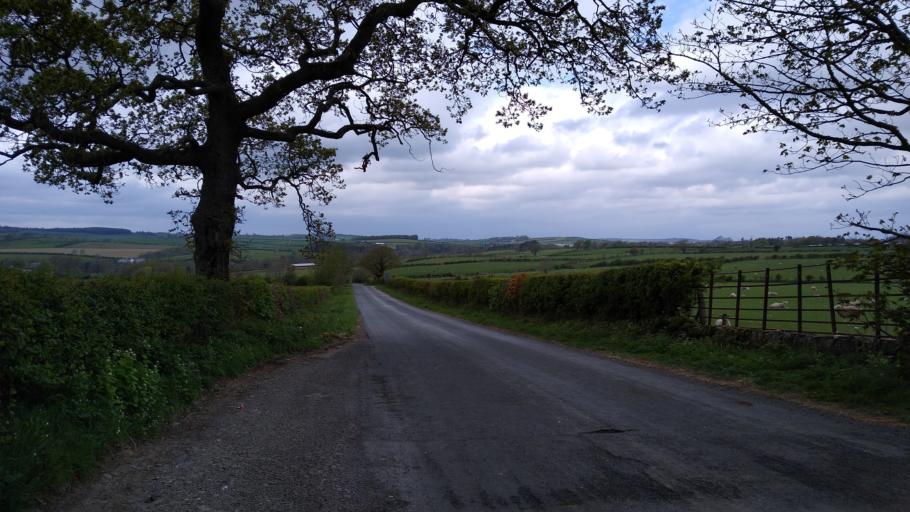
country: GB
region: England
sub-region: Cumbria
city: Cockermouth
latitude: 54.6435
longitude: -3.3359
